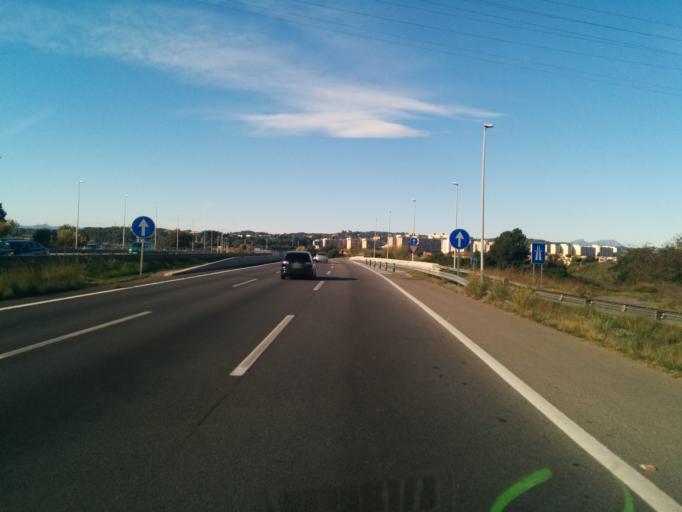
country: ES
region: Catalonia
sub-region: Provincia de Barcelona
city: Barbera del Valles
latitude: 41.5057
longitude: 2.1314
